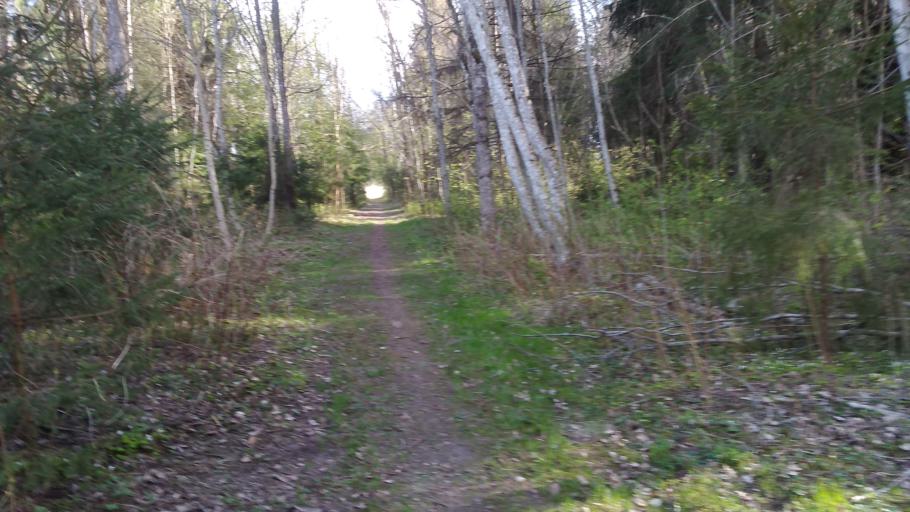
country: EE
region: Harju
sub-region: Saue linn
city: Saue
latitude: 59.2456
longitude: 24.5006
